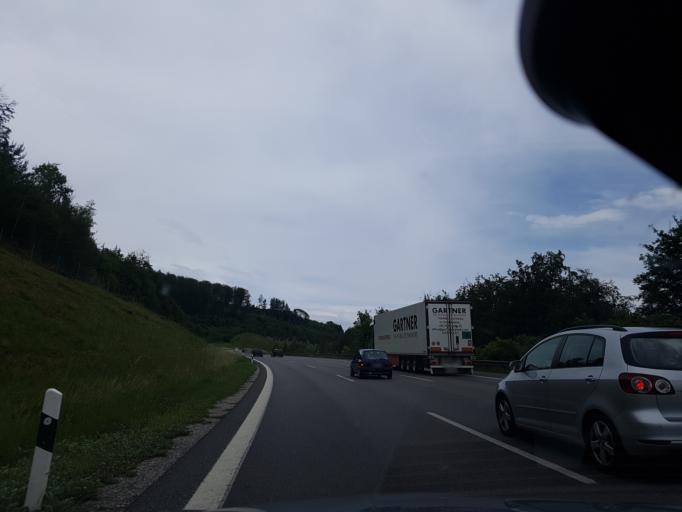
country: DE
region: Bavaria
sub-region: Regierungsbezirk Mittelfranken
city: Simmelsdorf
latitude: 49.5873
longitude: 11.3537
